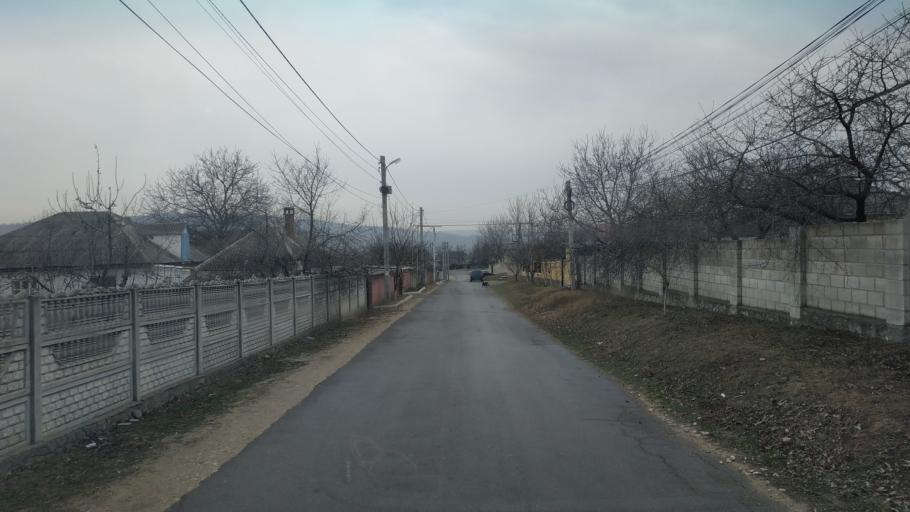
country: MD
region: Chisinau
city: Singera
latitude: 46.9184
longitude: 28.9593
